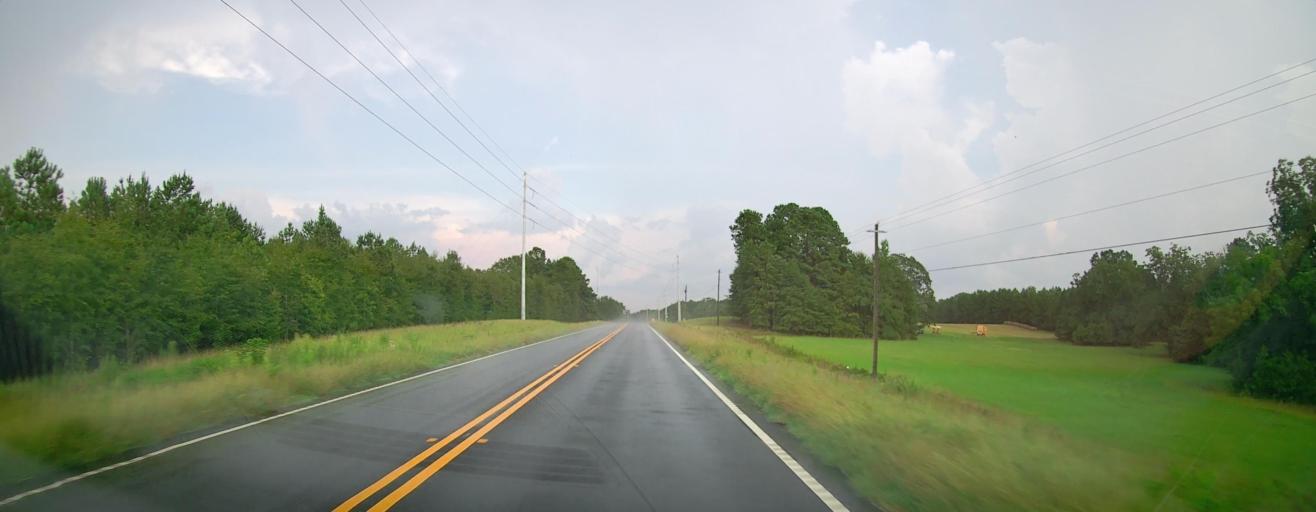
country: US
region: Georgia
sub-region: Twiggs County
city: Jeffersonville
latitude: 32.5772
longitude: -83.2062
